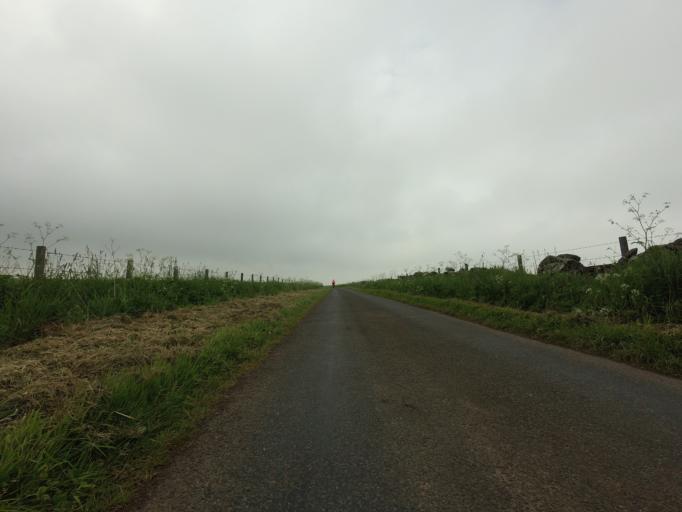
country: GB
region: Scotland
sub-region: Perth and Kinross
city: Milnathort
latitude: 56.2452
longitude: -3.3402
